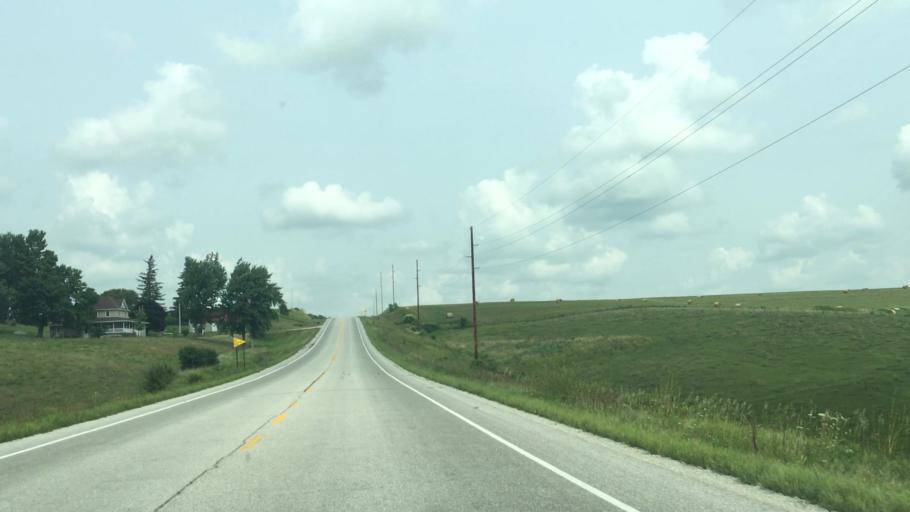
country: US
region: Minnesota
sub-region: Fillmore County
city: Harmony
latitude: 43.5753
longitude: -91.9298
